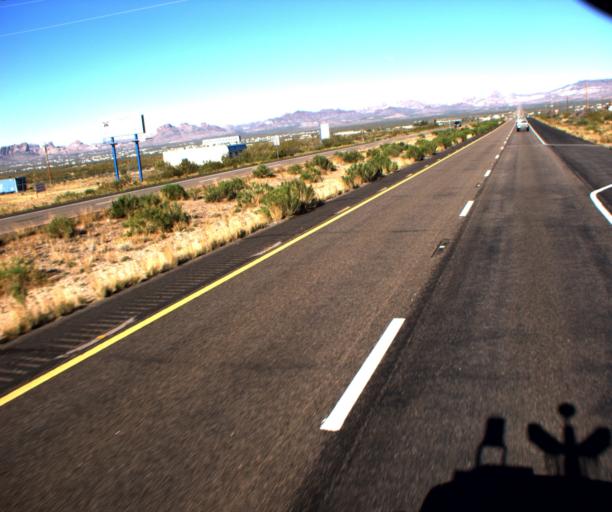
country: US
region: Arizona
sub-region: Mohave County
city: Golden Valley
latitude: 35.2243
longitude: -114.2600
